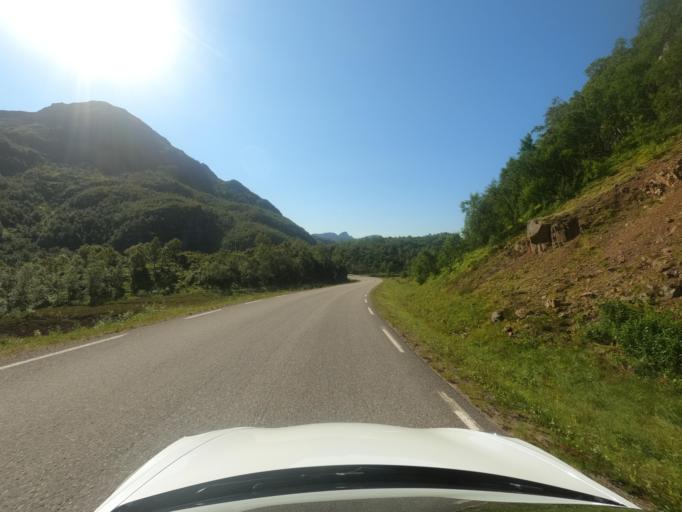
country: NO
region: Nordland
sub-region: Sortland
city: Sortland
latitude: 68.4542
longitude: 15.2049
